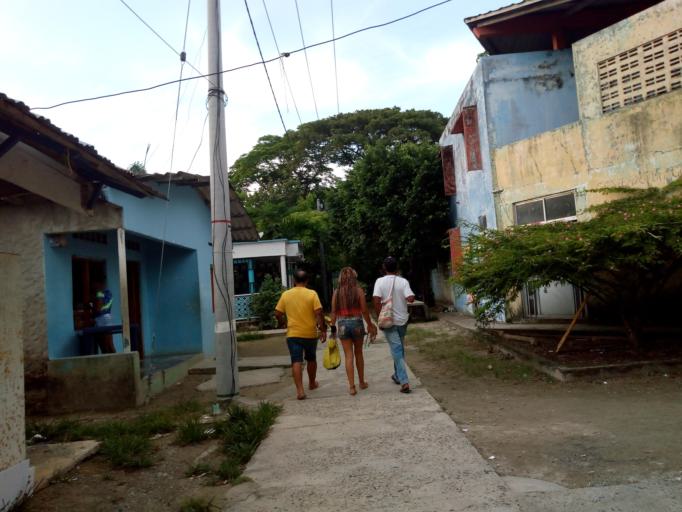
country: PA
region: Guna Yala
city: Puerto Obaldia
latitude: 8.6611
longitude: -77.3653
